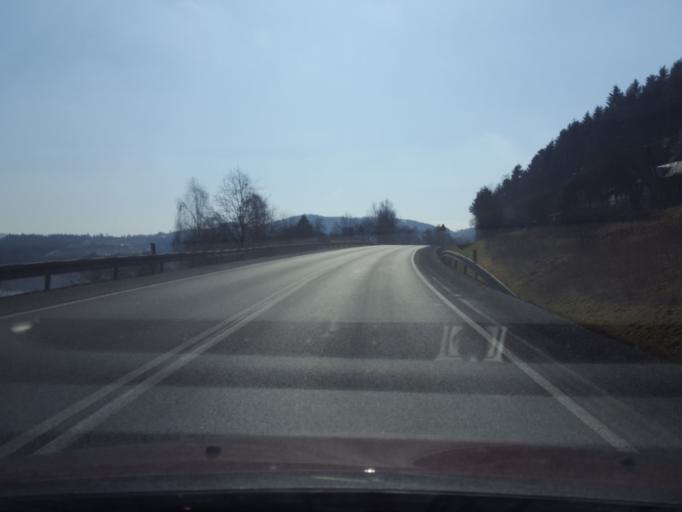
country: PL
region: Lesser Poland Voivodeship
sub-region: Powiat nowosadecki
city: Lososina Dolna
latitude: 49.7932
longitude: 20.6471
